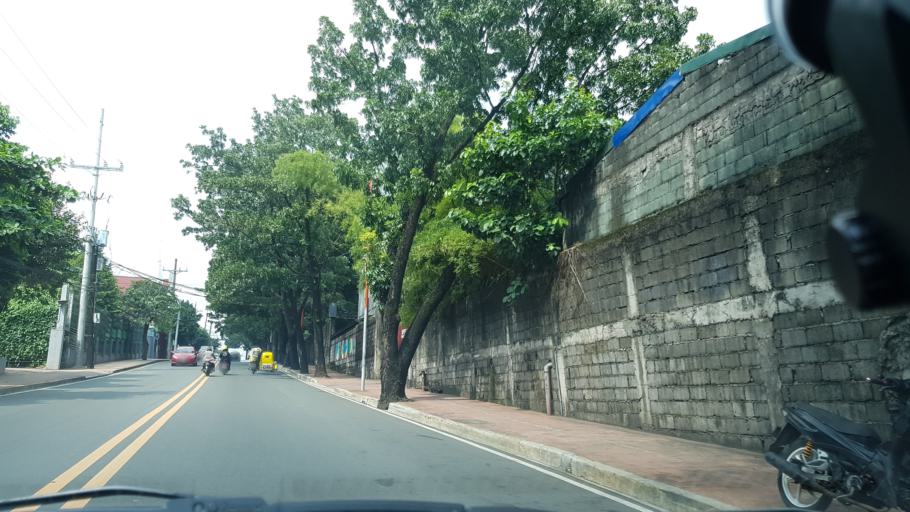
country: PH
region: Calabarzon
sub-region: Province of Rizal
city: Antipolo
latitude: 14.6576
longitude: 121.1183
